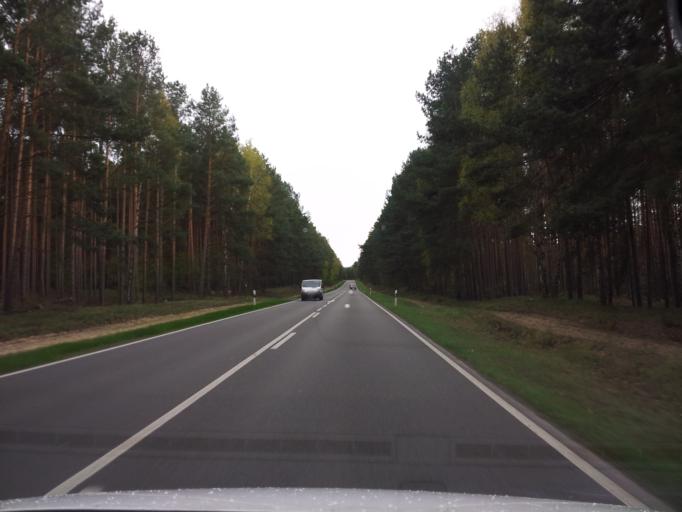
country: DE
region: Brandenburg
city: Heinersbruck
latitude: 51.7254
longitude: 14.4588
